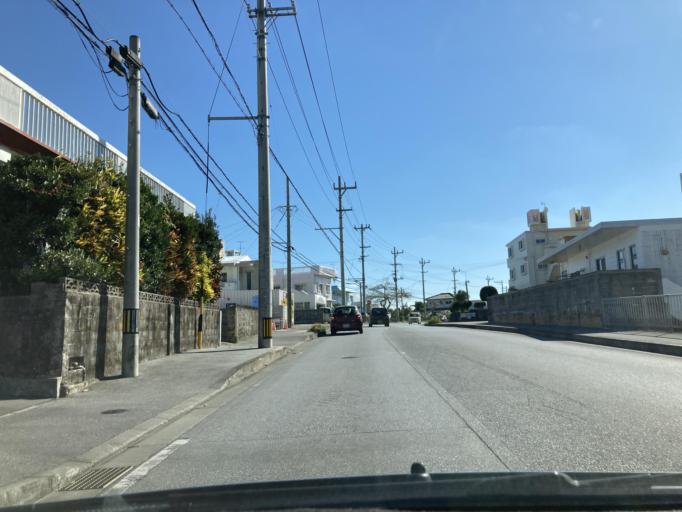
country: JP
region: Okinawa
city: Okinawa
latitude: 26.3620
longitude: 127.8247
